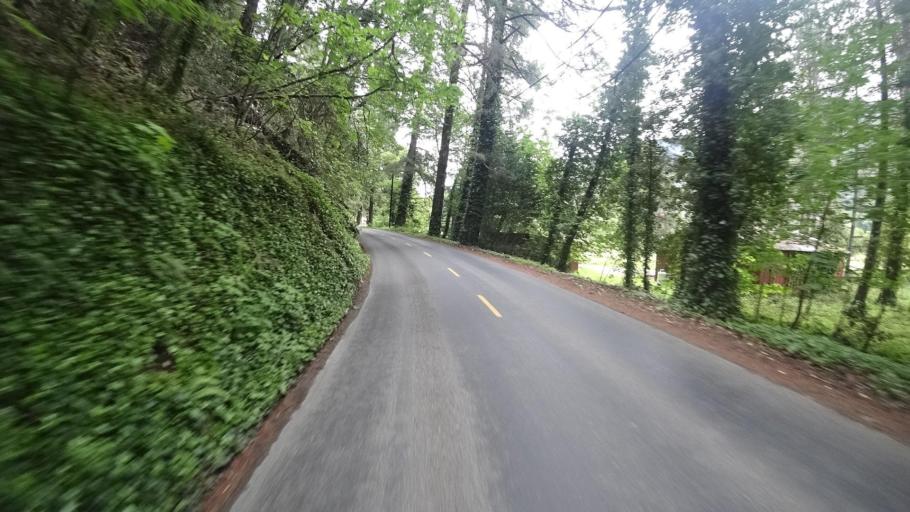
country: US
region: California
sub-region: Humboldt County
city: Willow Creek
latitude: 40.9519
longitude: -123.6300
